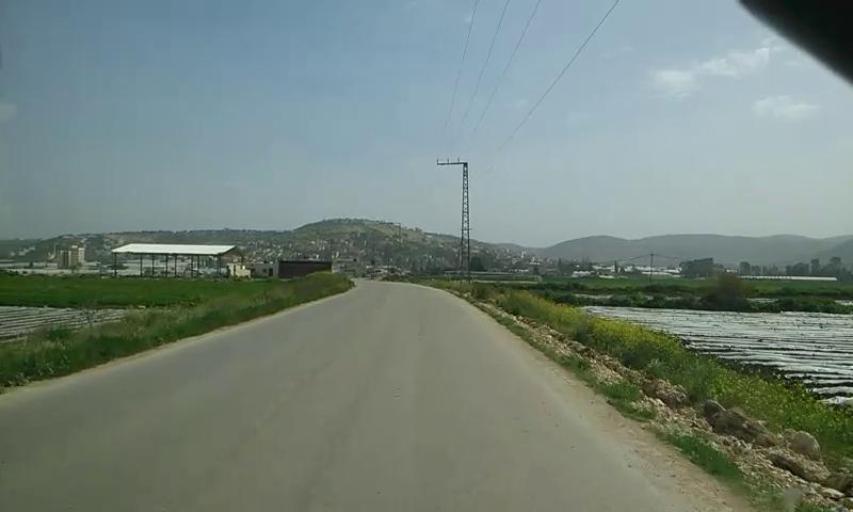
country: PS
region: West Bank
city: Ash Shuhada'
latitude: 32.4351
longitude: 35.2660
